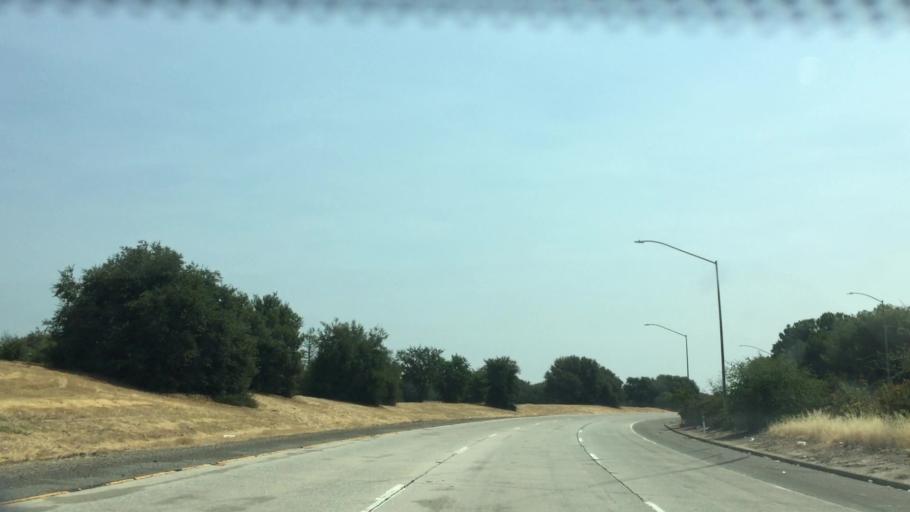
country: US
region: California
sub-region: Sacramento County
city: North Highlands
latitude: 38.6468
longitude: -121.3736
